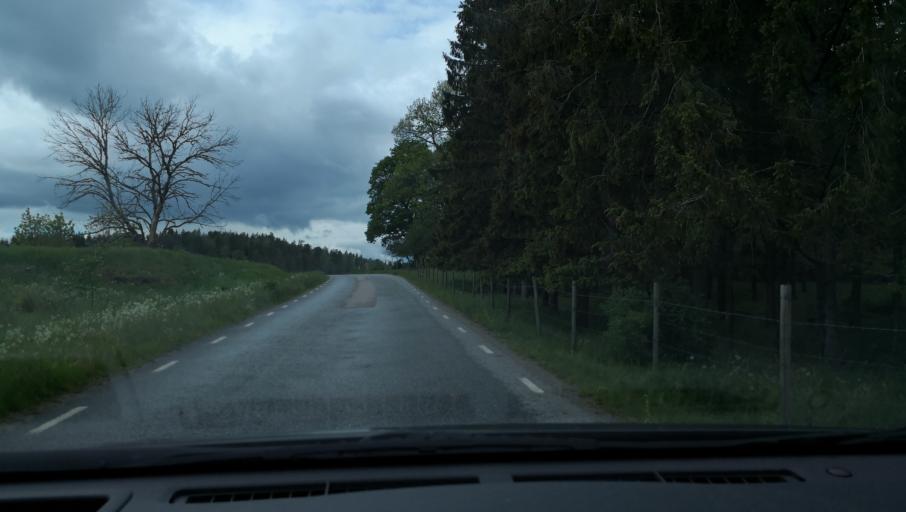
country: SE
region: Uppsala
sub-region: Enkopings Kommun
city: Orsundsbro
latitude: 59.7239
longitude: 17.3900
